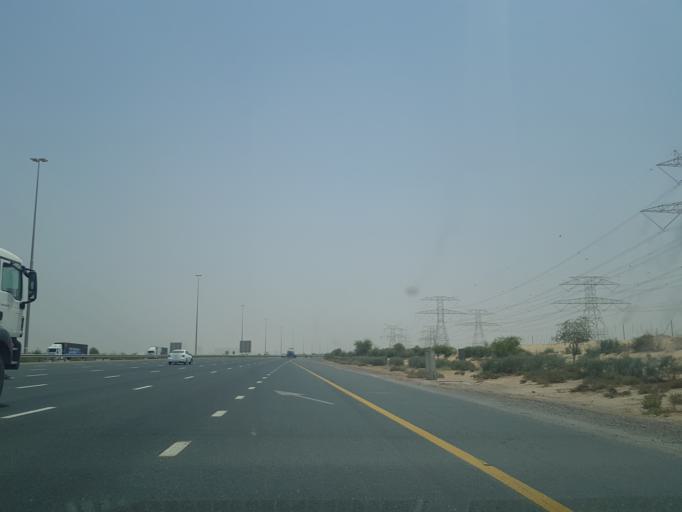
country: AE
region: Dubai
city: Dubai
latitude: 25.0619
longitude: 55.3260
